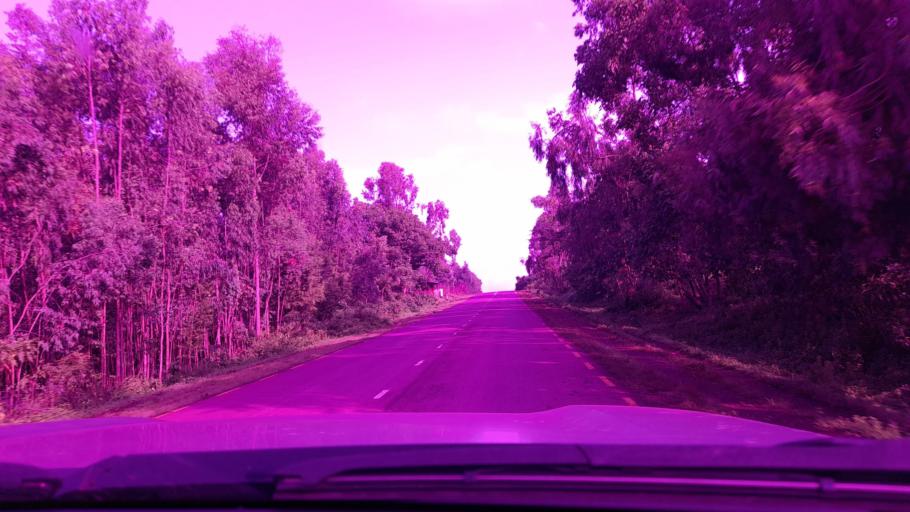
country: ET
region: Oromiya
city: Bedele
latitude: 8.1870
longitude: 36.4486
